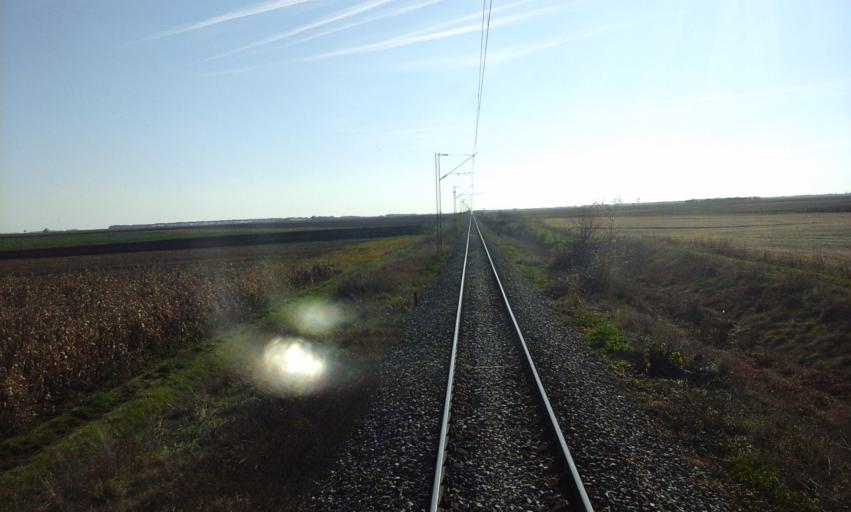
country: RS
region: Autonomna Pokrajina Vojvodina
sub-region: Severnobacki Okrug
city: Backa Topola
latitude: 45.9132
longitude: 19.6642
